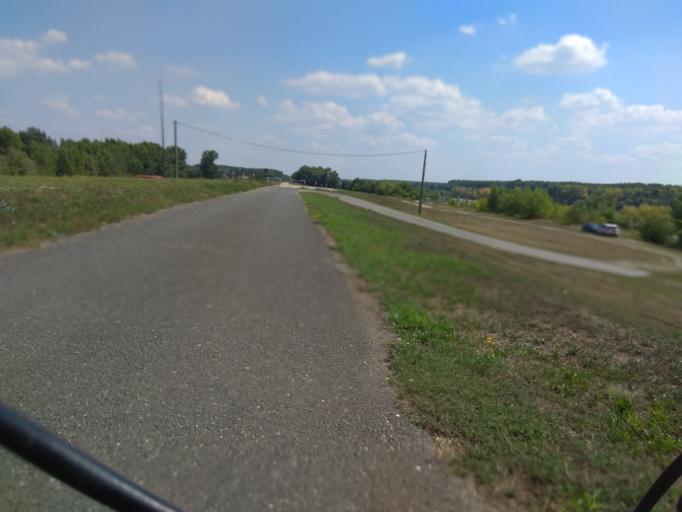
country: SK
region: Trnavsky
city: Gabcikovo
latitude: 47.8257
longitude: 17.6069
